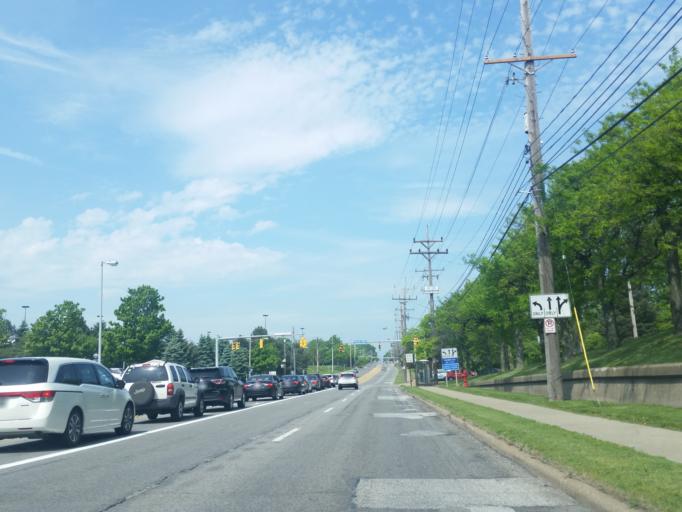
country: US
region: Ohio
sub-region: Cuyahoga County
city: Lyndhurst
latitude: 41.5012
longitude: -81.4896
